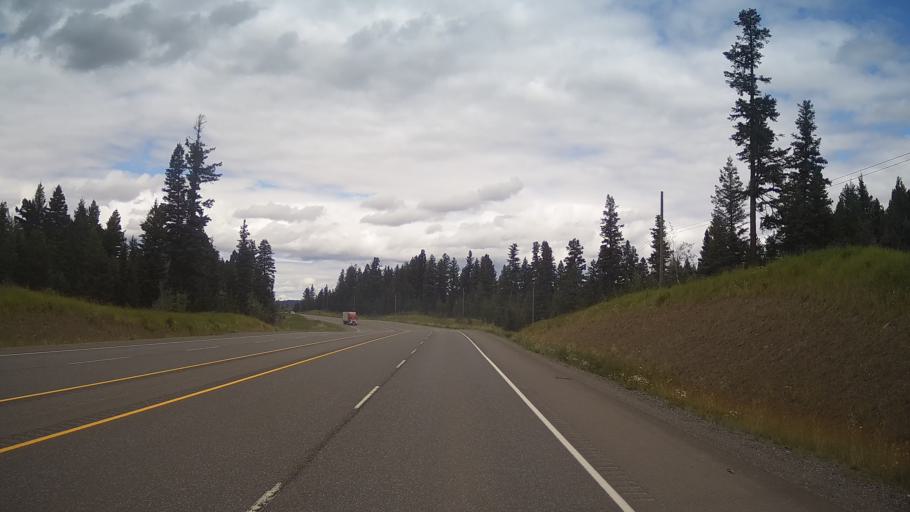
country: CA
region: British Columbia
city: Cache Creek
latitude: 51.4070
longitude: -121.3747
